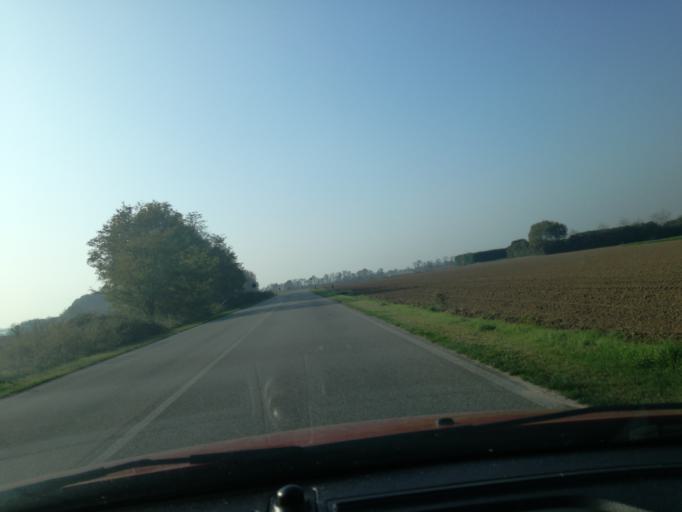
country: IT
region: Lombardy
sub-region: Provincia di Monza e Brianza
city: Ornago
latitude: 45.5935
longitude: 9.4136
